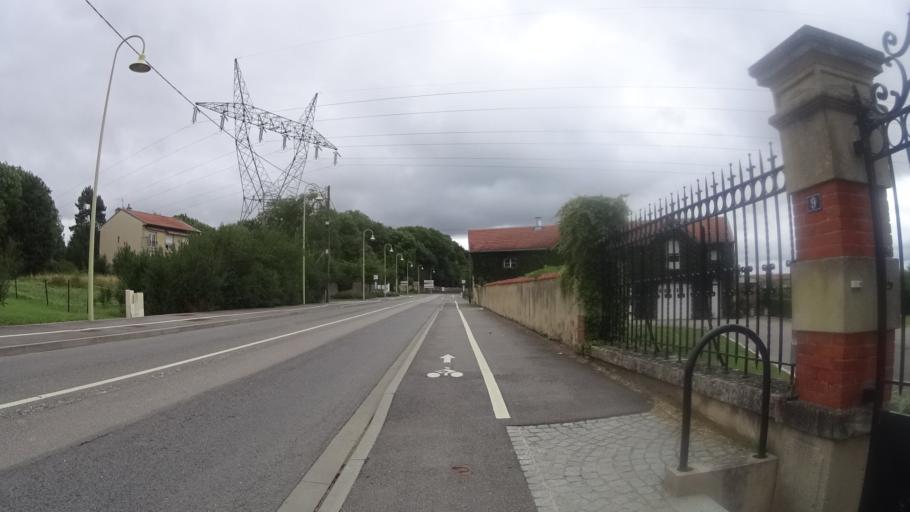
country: FR
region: Lorraine
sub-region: Departement de Meurthe-et-Moselle
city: Art-sur-Meurthe
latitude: 48.6582
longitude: 6.2613
